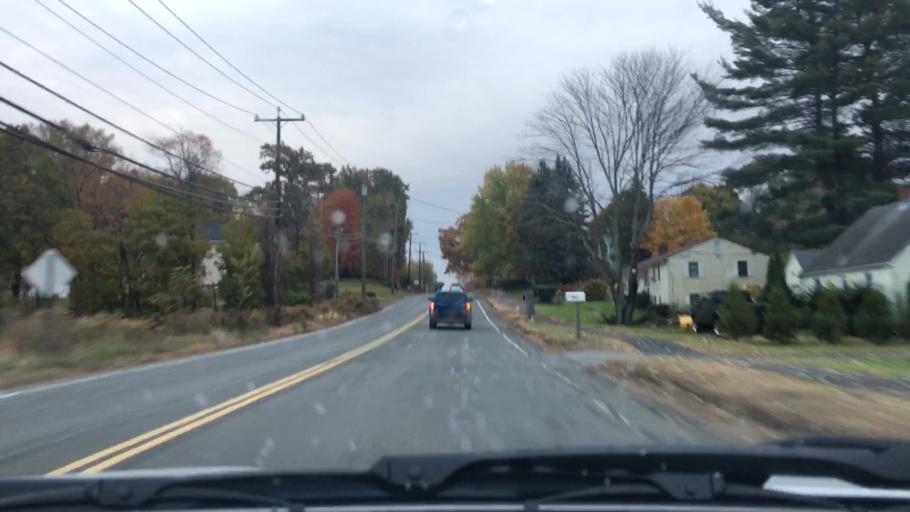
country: US
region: Massachusetts
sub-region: Hampden County
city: Agawam
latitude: 42.0660
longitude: -72.6901
